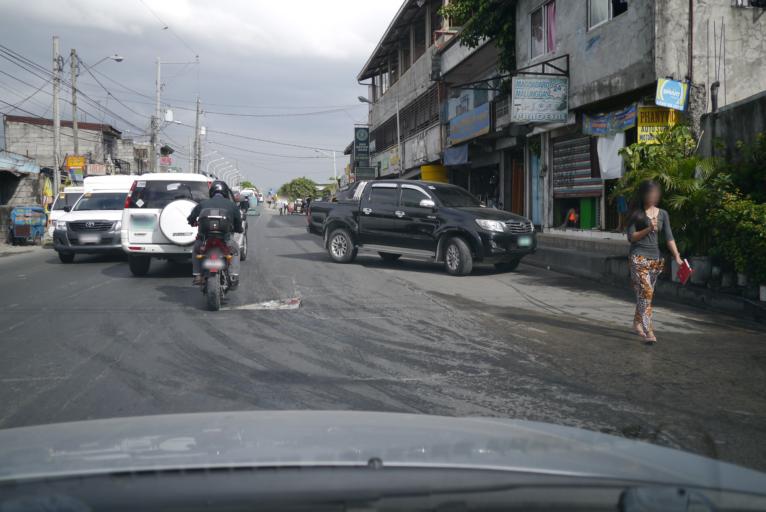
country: PH
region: Calabarzon
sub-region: Province of Rizal
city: Cainta
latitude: 14.5631
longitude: 121.1109
